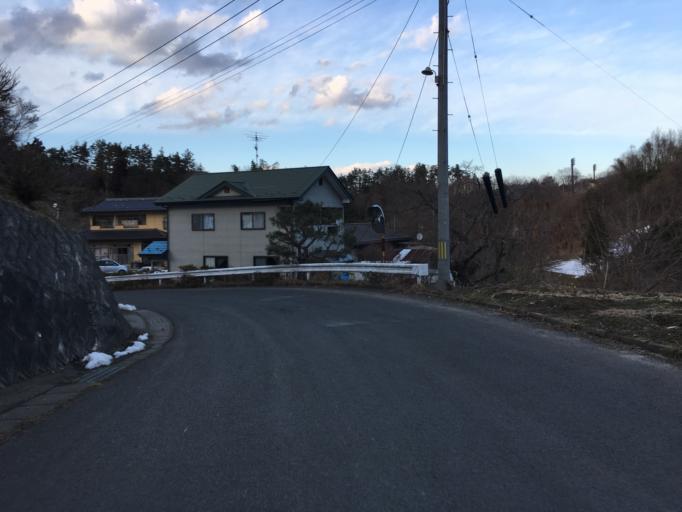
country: JP
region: Fukushima
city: Fukushima-shi
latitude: 37.6514
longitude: 140.5885
